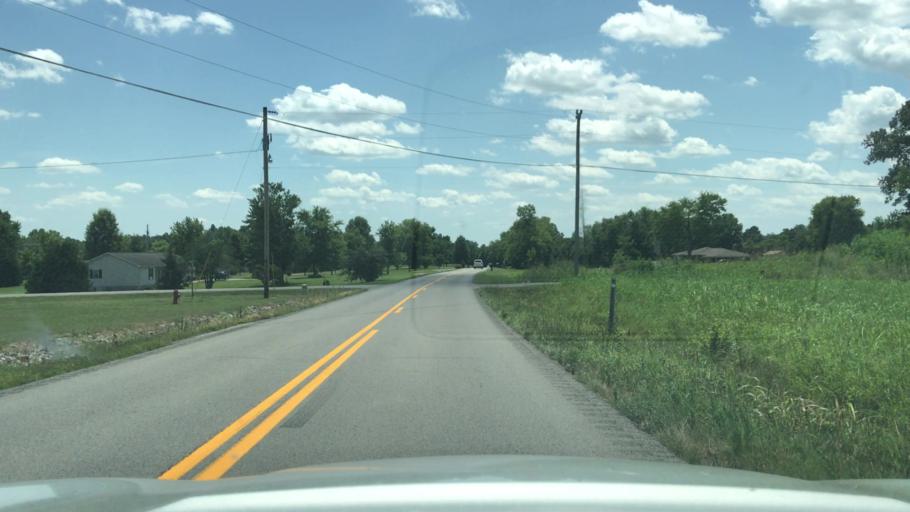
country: US
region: Kentucky
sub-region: Christian County
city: Hopkinsville
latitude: 36.9164
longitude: -87.4397
